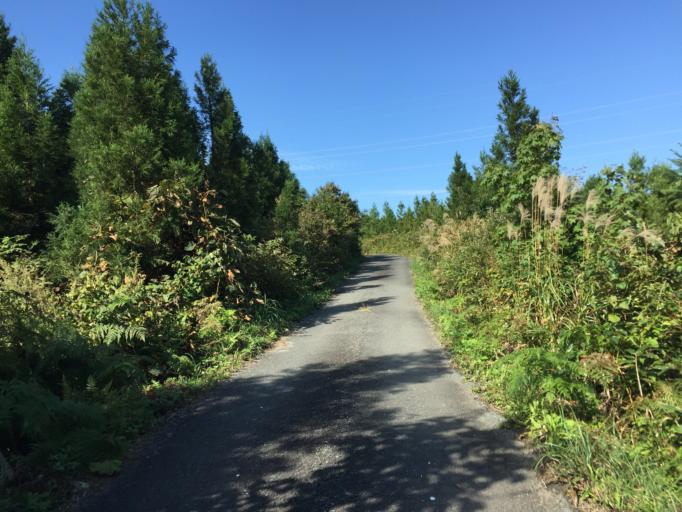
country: JP
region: Yamagata
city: Yonezawa
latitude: 37.8161
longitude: 140.2490
